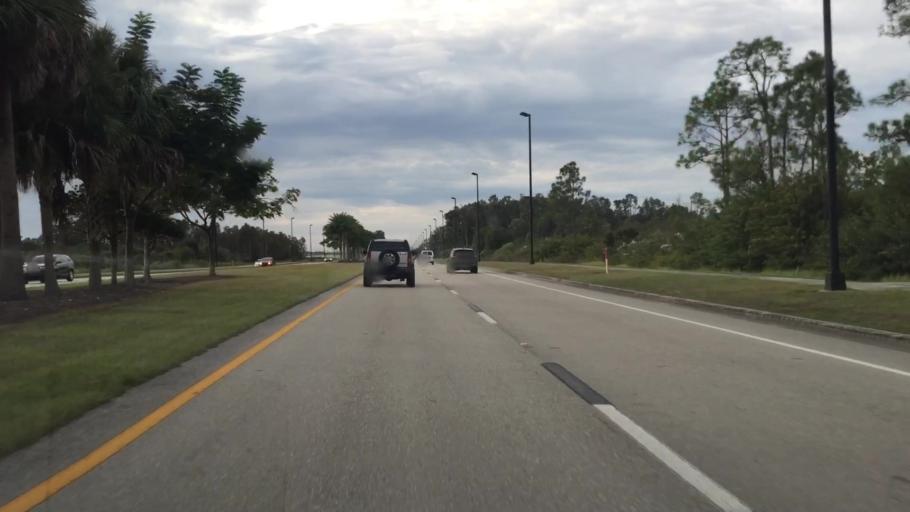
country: US
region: Florida
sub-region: Lee County
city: Three Oaks
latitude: 26.5244
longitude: -81.7856
